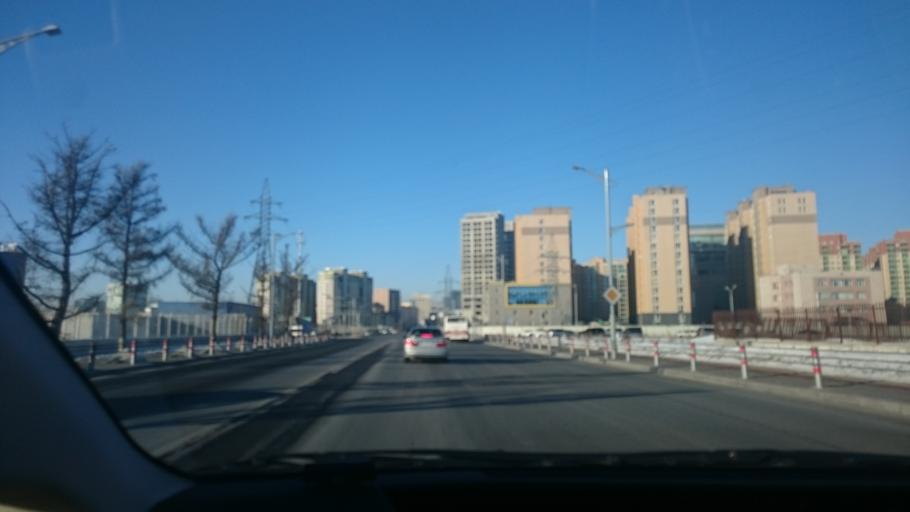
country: MN
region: Ulaanbaatar
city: Ulaanbaatar
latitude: 47.8988
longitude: 106.9317
